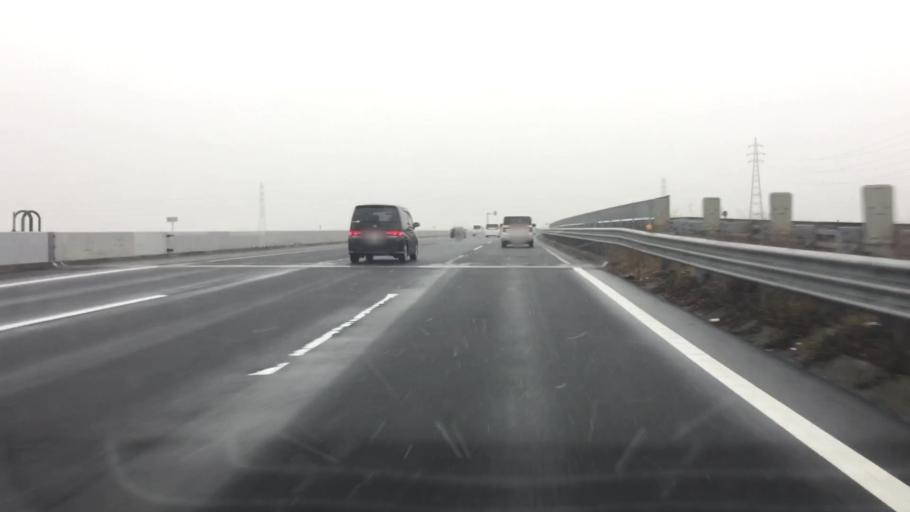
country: JP
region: Tochigi
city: Fujioka
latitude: 36.2664
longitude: 139.6007
